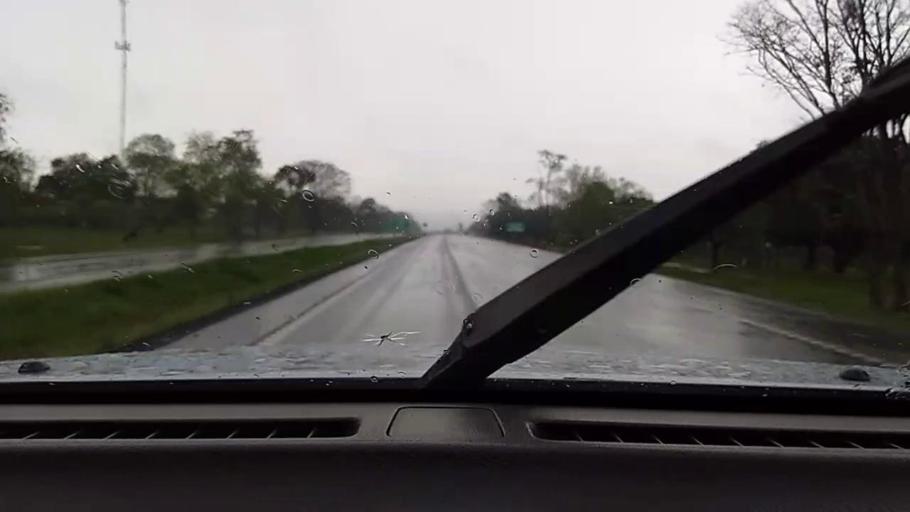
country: PY
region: Caaguazu
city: Repatriacion
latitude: -25.4530
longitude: -55.9066
